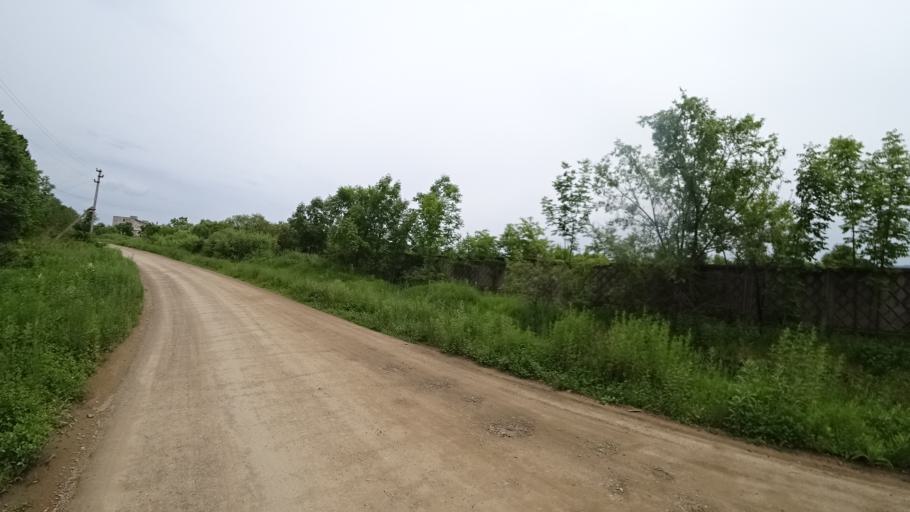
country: RU
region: Primorskiy
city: Arsen'yev
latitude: 44.1976
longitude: 133.3079
